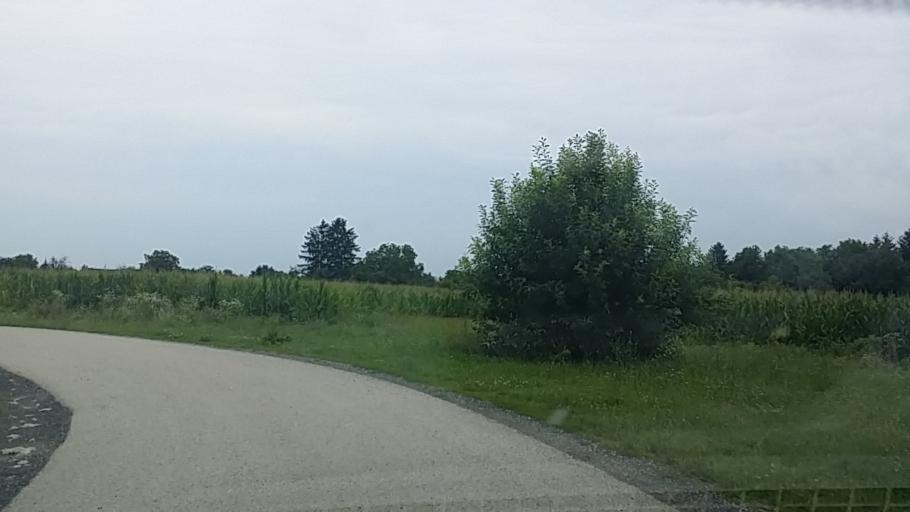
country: HR
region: Medimurska
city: Domasinec
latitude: 46.4753
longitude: 16.6397
